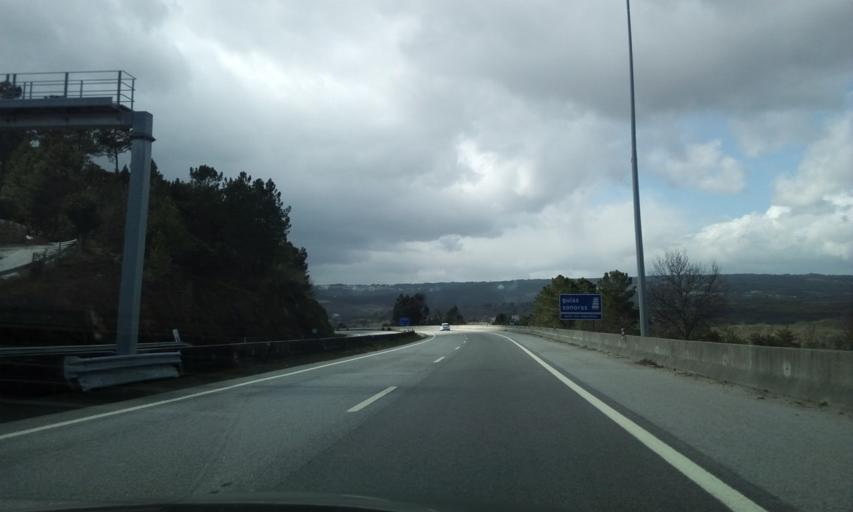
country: PT
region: Viseu
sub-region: Mangualde
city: Mangualde
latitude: 40.6323
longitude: -7.8059
